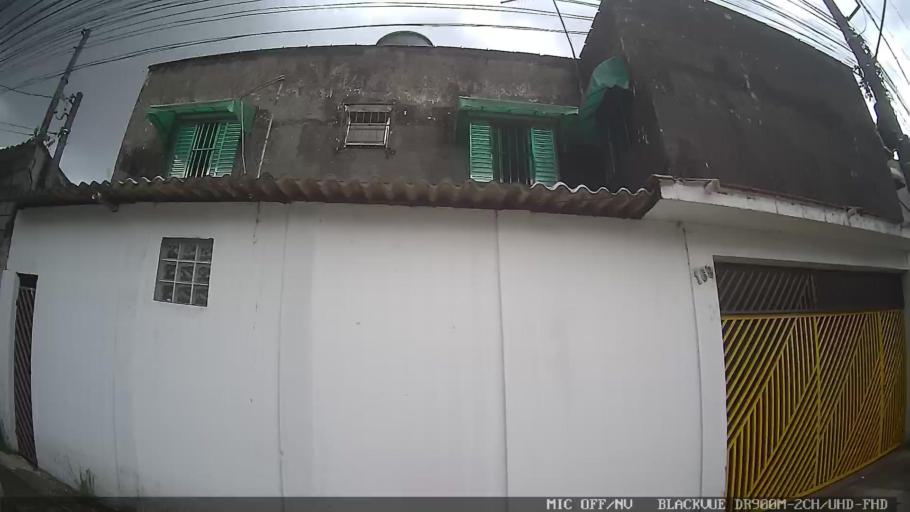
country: BR
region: Sao Paulo
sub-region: Suzano
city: Suzano
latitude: -23.5681
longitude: -46.2948
